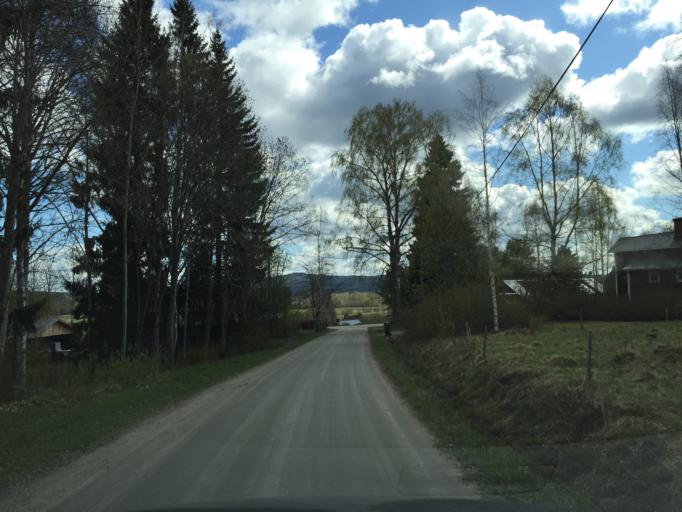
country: SE
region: Gaevleborg
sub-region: Bollnas Kommun
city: Arbra
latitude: 61.5201
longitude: 16.3464
